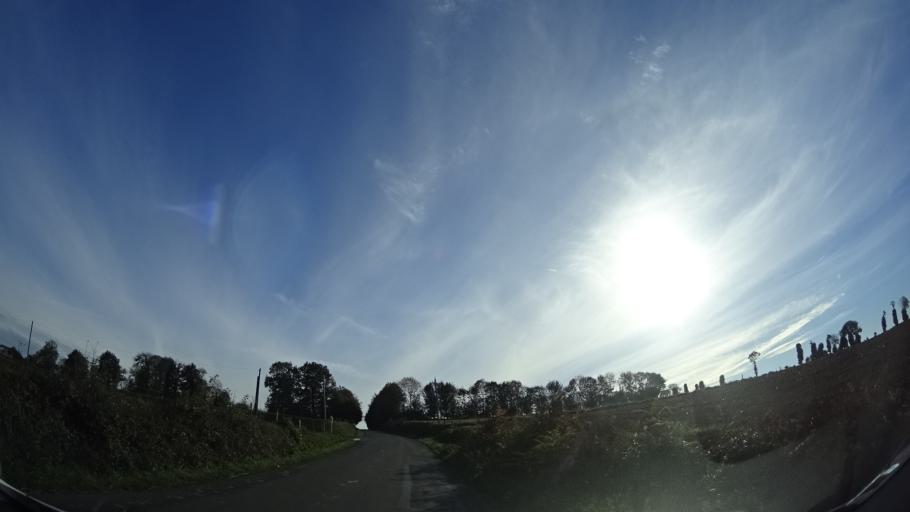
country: FR
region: Brittany
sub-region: Departement d'Ille-et-Vilaine
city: Geveze
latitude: 48.2156
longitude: -1.8268
